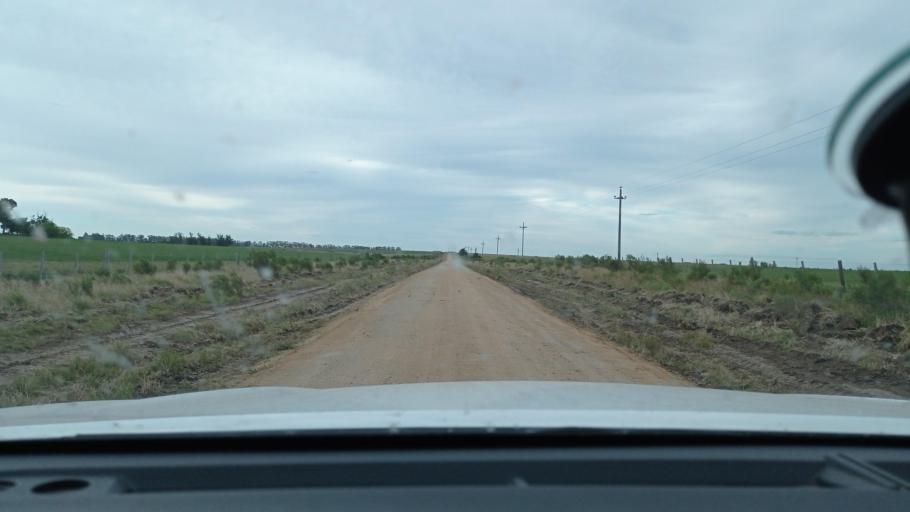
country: UY
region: Florida
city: Casupa
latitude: -34.1069
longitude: -55.7639
